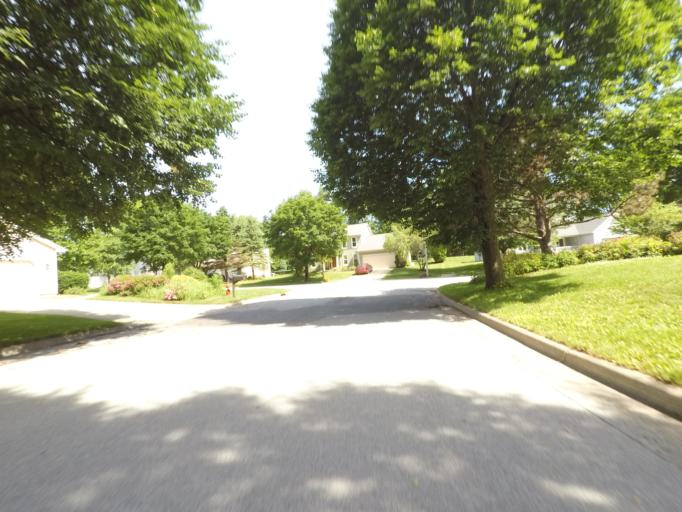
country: US
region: Wisconsin
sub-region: Dane County
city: Middleton
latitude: 43.0816
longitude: -89.5149
